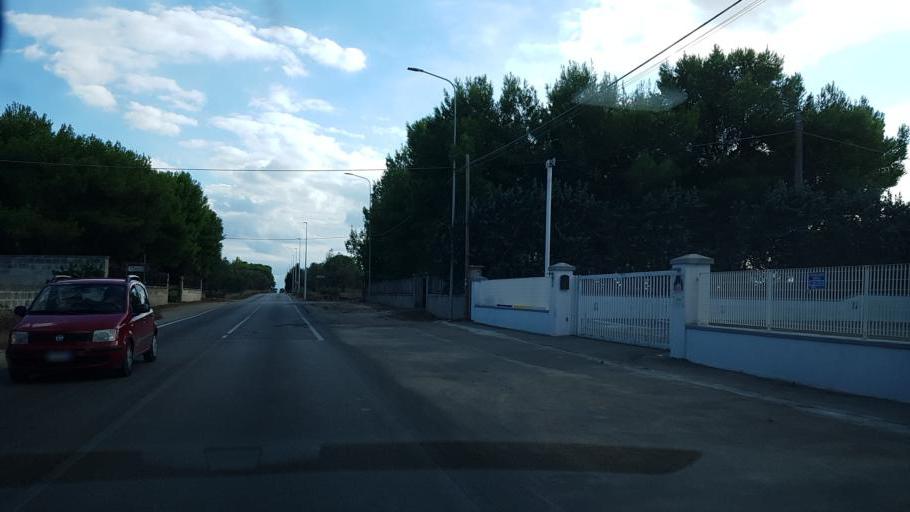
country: IT
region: Apulia
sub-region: Provincia di Lecce
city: Nardo
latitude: 40.1437
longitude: 18.0186
